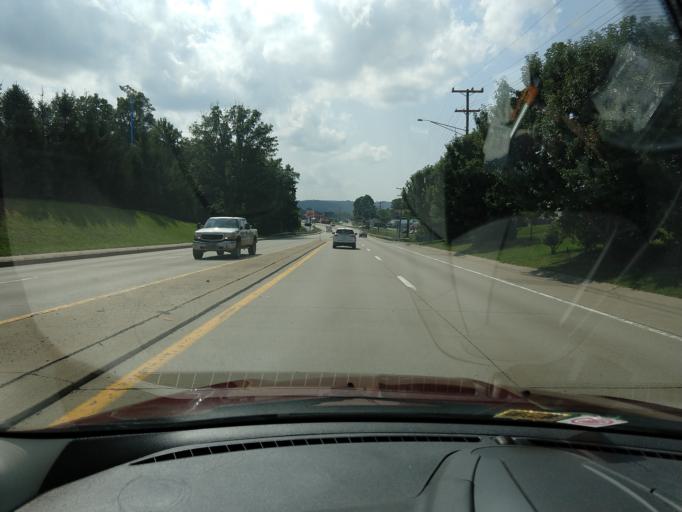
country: US
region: Pennsylvania
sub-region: Greene County
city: Morrisville
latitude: 39.8979
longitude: -80.1572
